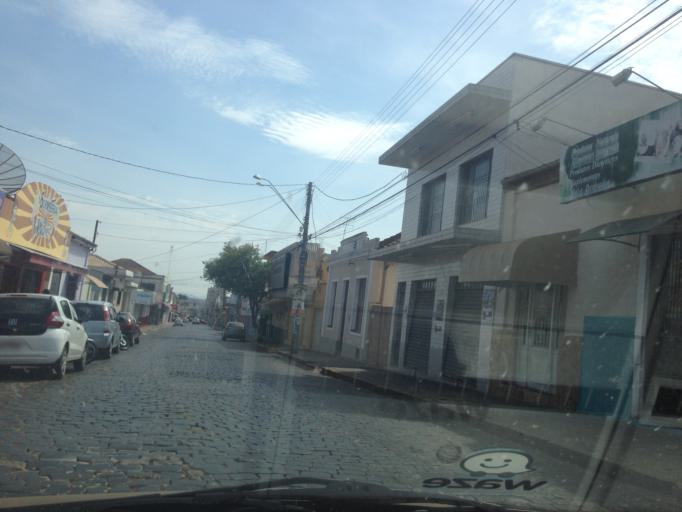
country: BR
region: Sao Paulo
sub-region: Casa Branca
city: Casa Branca
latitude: -21.7767
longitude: -47.0812
